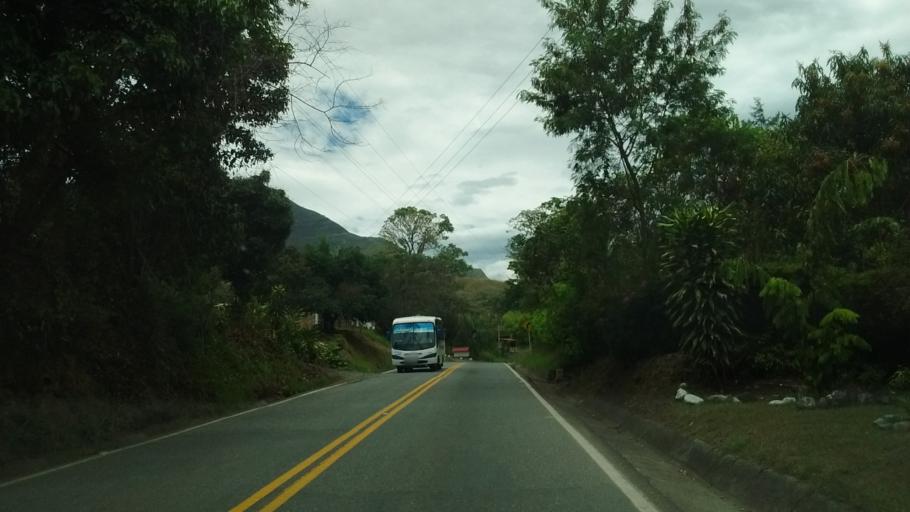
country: CO
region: Cauca
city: Rosas
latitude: 2.2369
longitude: -76.7855
